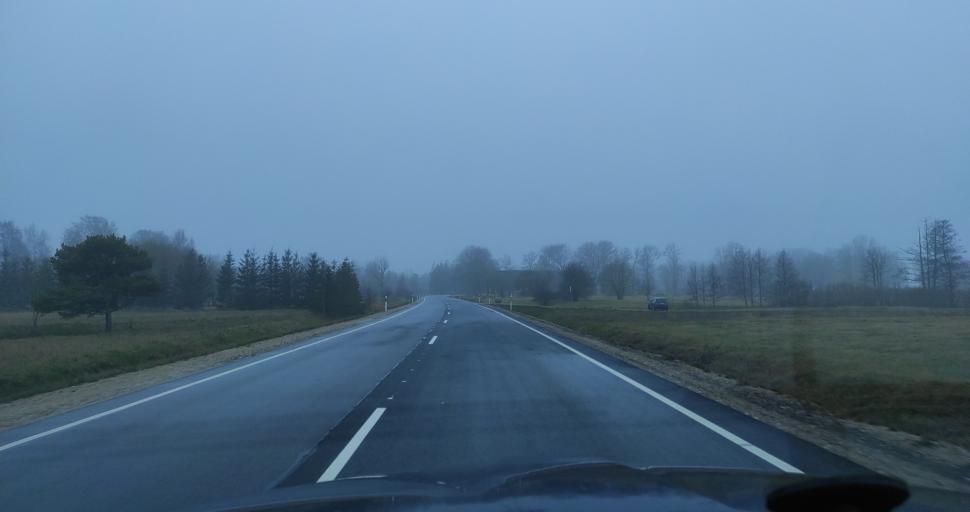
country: LV
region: Pavilostas
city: Pavilosta
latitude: 56.9166
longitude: 21.2469
